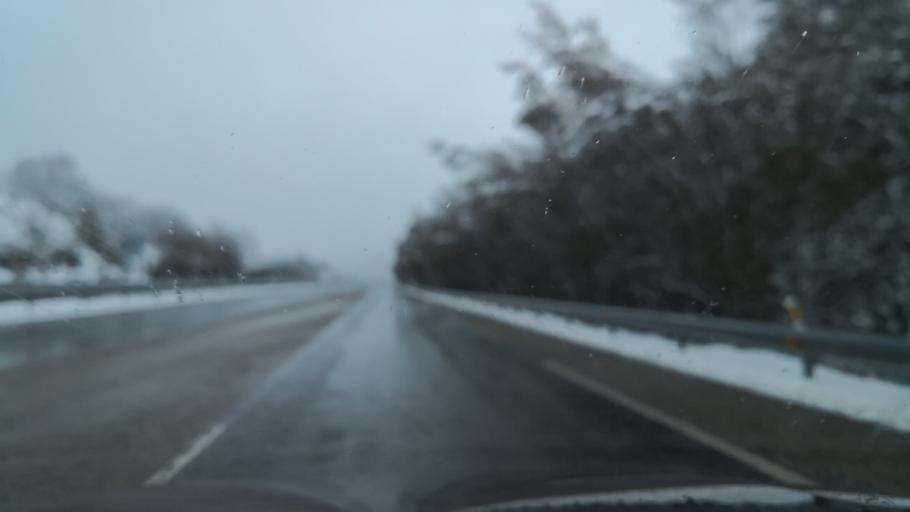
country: ES
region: Castille and Leon
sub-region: Provincia de Zamora
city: Lubian
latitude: 42.0281
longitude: -6.8965
